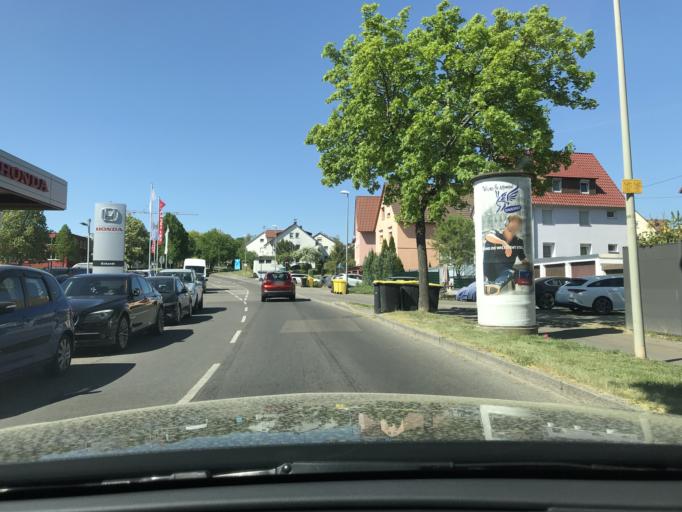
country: DE
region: Baden-Wuerttemberg
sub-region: Regierungsbezirk Stuttgart
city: Korb
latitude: 48.8386
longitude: 9.3645
